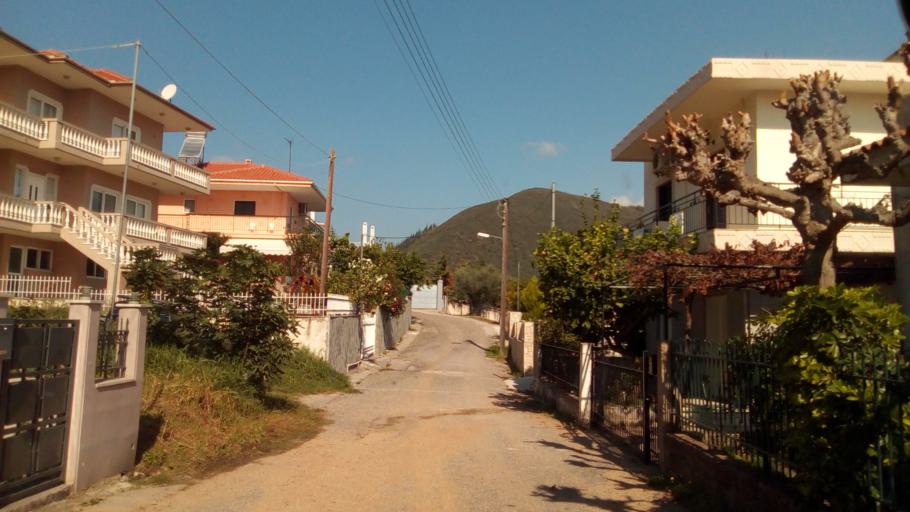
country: GR
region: West Greece
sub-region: Nomos Aitolias kai Akarnanias
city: Antirrio
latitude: 38.3667
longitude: 21.7745
